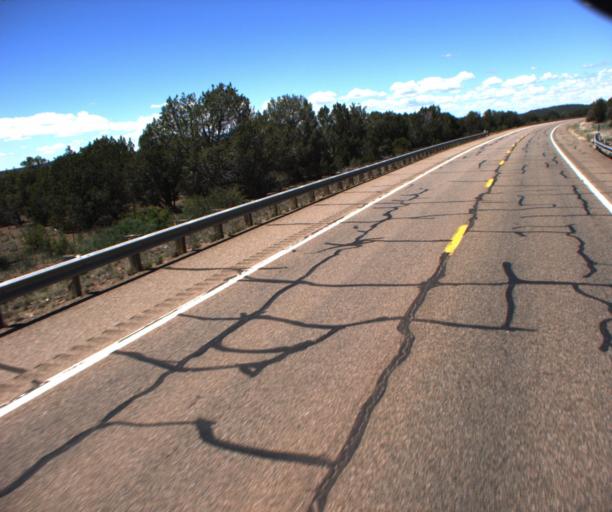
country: US
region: Arizona
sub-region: Yavapai County
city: Paulden
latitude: 35.1060
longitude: -112.4284
